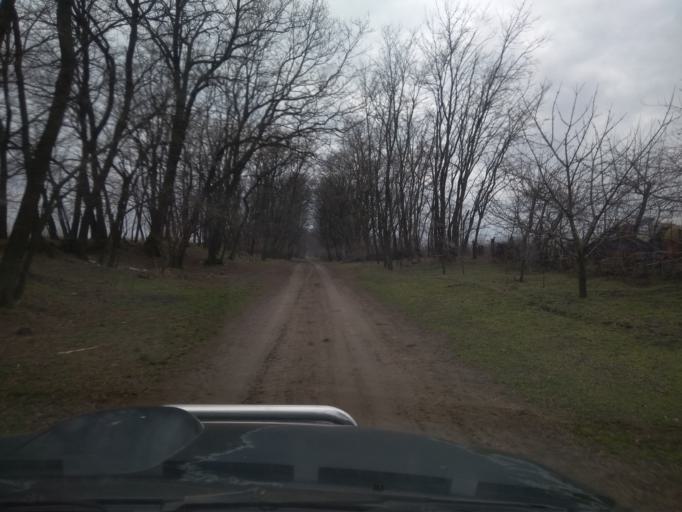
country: HU
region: Szabolcs-Szatmar-Bereg
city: Nyirtelek
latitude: 47.9681
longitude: 21.6470
